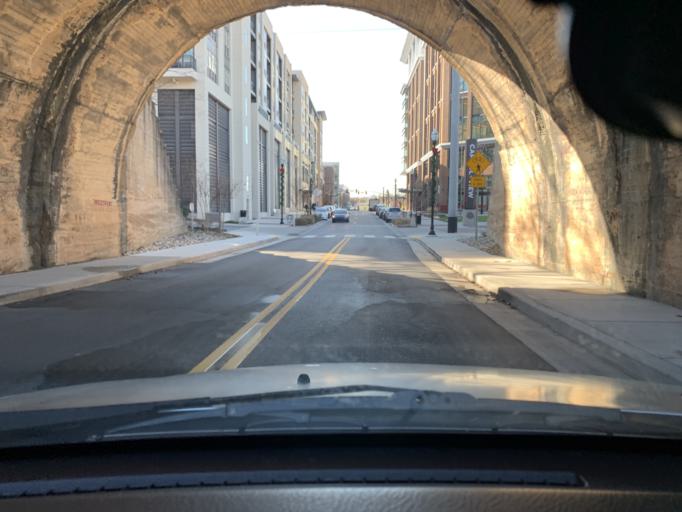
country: US
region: Tennessee
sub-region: Davidson County
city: Nashville
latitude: 36.1643
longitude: -86.7896
